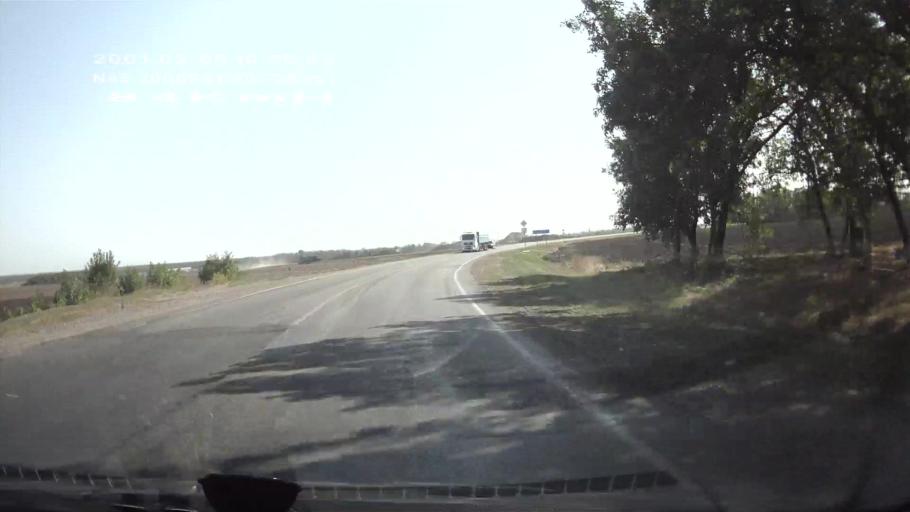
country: RU
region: Krasnodarskiy
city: Dmitriyevskaya
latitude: 45.7005
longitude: 40.7405
